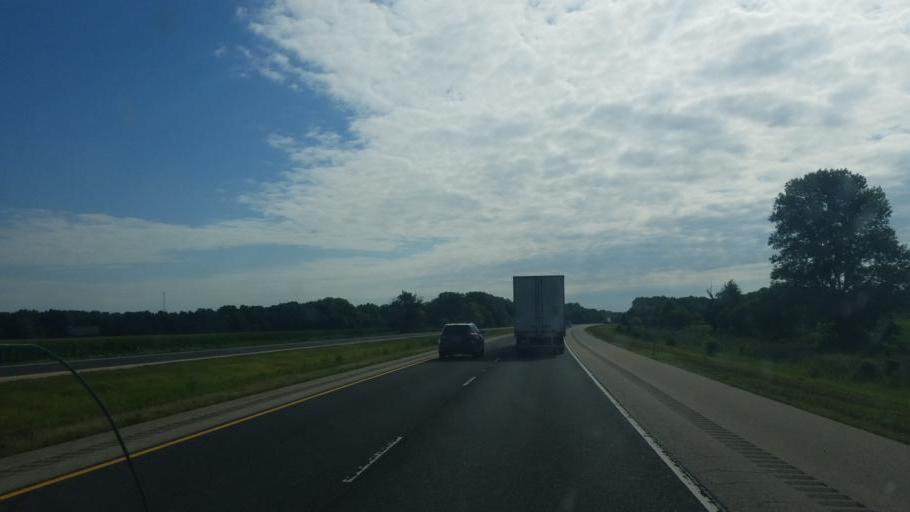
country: US
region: Illinois
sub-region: Clark County
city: Marshall
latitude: 39.4009
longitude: -87.7656
